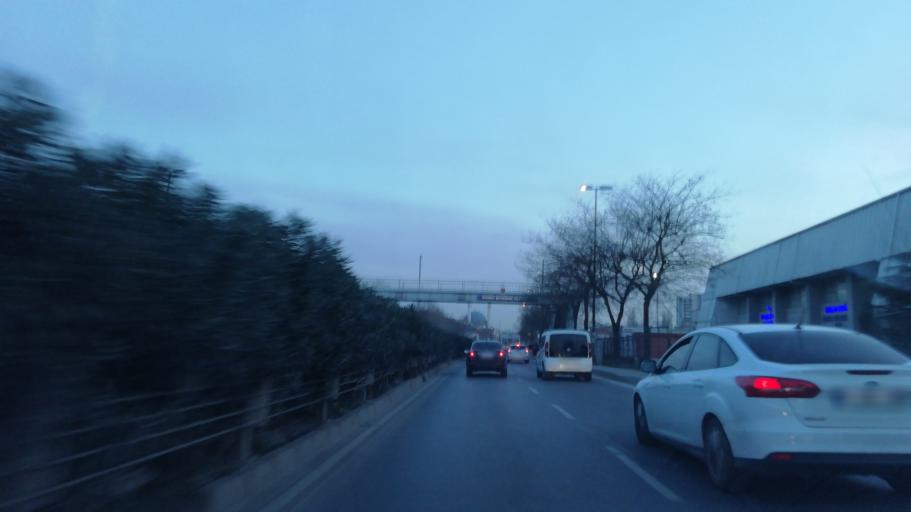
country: TR
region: Istanbul
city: Bahcelievler
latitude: 41.0194
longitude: 28.8486
